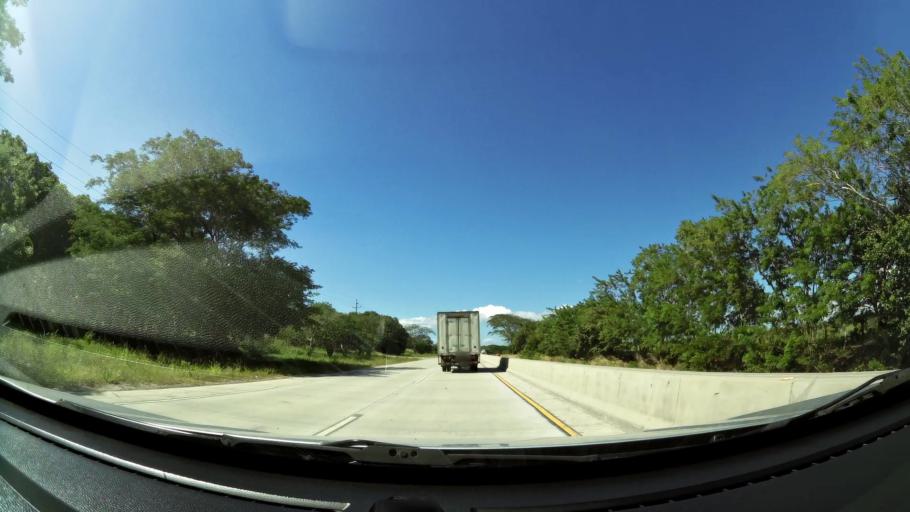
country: CR
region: Guanacaste
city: Liberia
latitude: 10.5841
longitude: -85.4123
